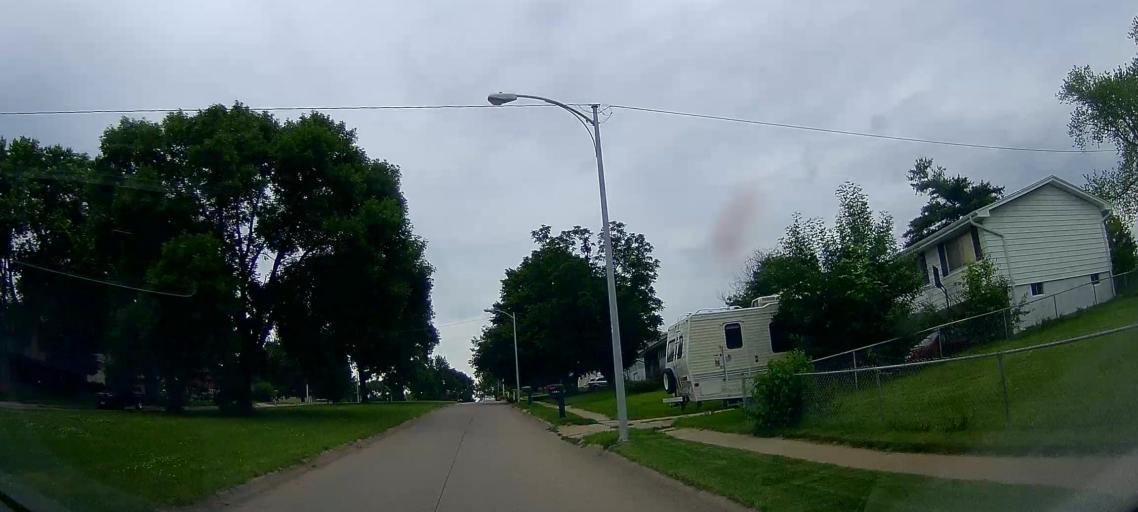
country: US
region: Nebraska
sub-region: Douglas County
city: Ralston
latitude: 41.3074
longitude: -96.0608
